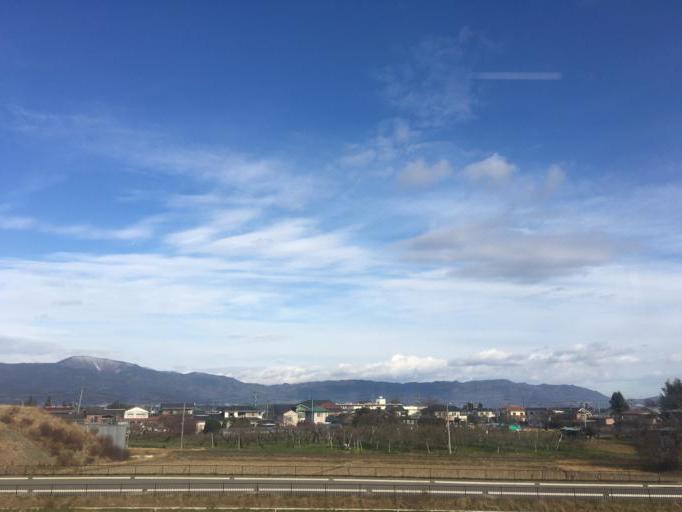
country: JP
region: Fukushima
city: Hobaramachi
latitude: 37.8096
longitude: 140.5402
